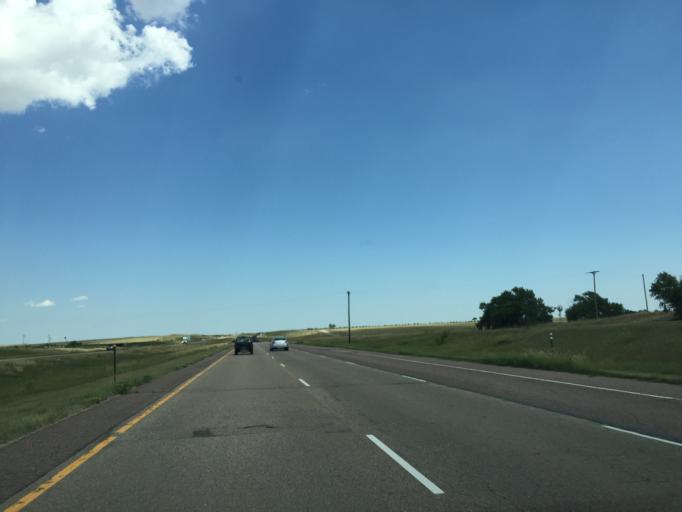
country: US
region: Colorado
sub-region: Lincoln County
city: Hugo
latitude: 39.2791
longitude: -103.3910
